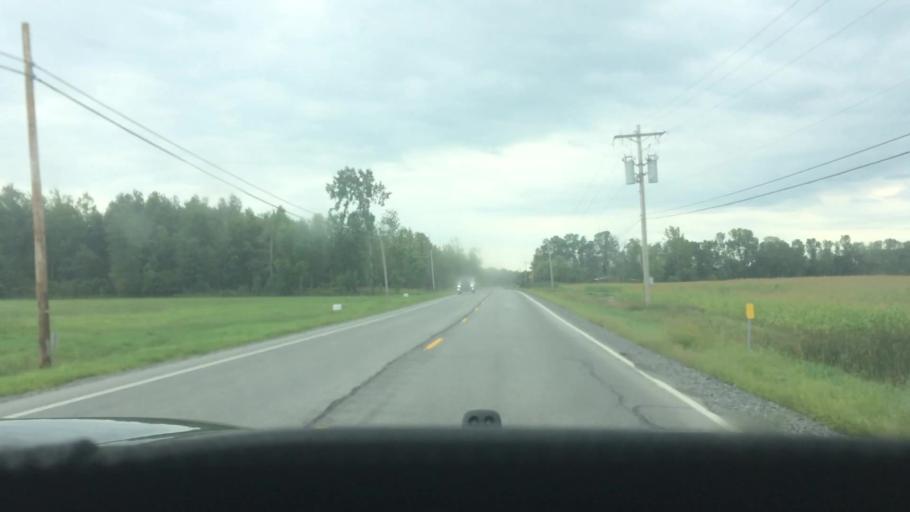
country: US
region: New York
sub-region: St. Lawrence County
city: Ogdensburg
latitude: 44.6317
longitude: -75.4242
